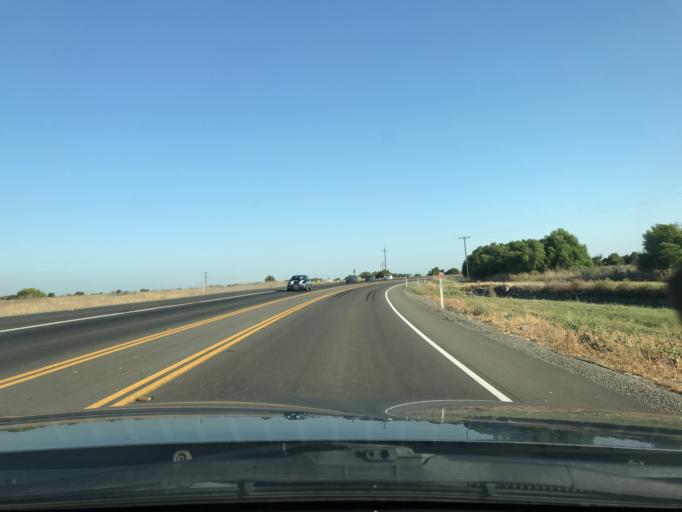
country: US
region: California
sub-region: Merced County
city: Los Banos
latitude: 37.1498
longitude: -120.8251
